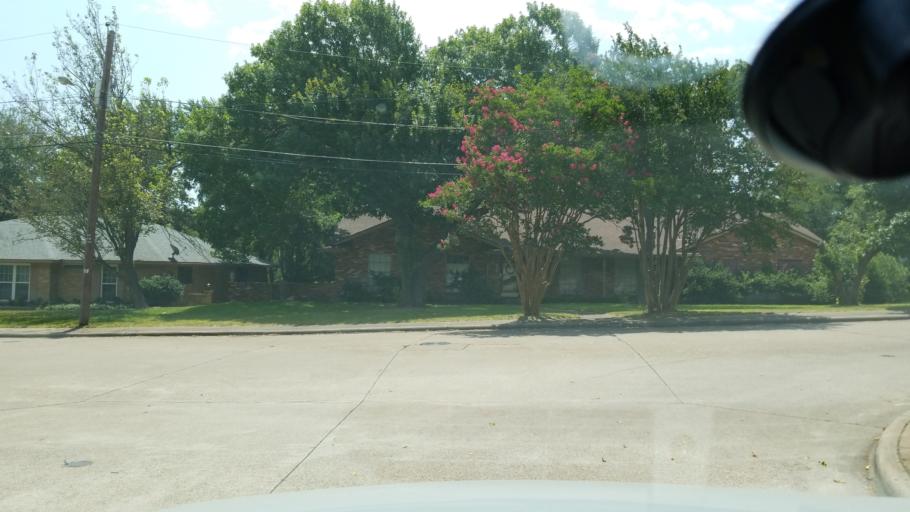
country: US
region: Texas
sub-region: Dallas County
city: Duncanville
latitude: 32.6736
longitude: -96.8382
